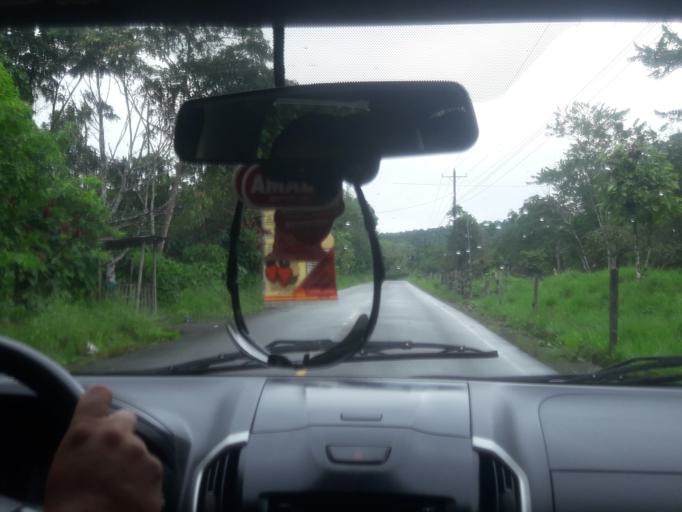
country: EC
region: Napo
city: Tena
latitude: -1.0339
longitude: -77.6838
